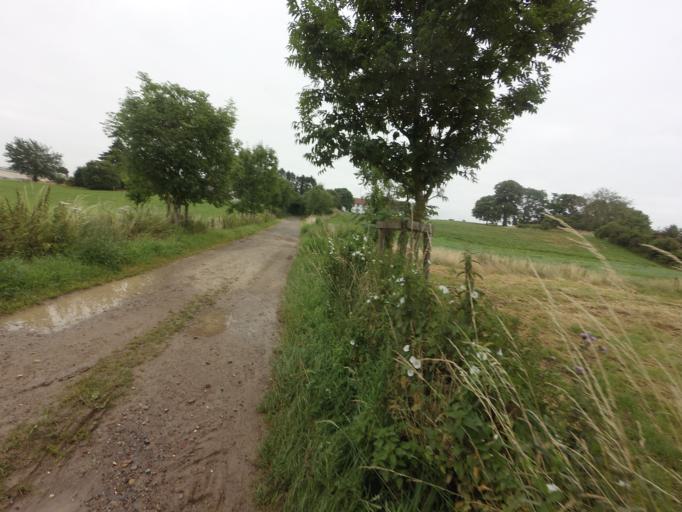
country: NL
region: Limburg
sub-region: Gemeente Vaals
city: Vaals
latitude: 50.7834
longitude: 5.9782
